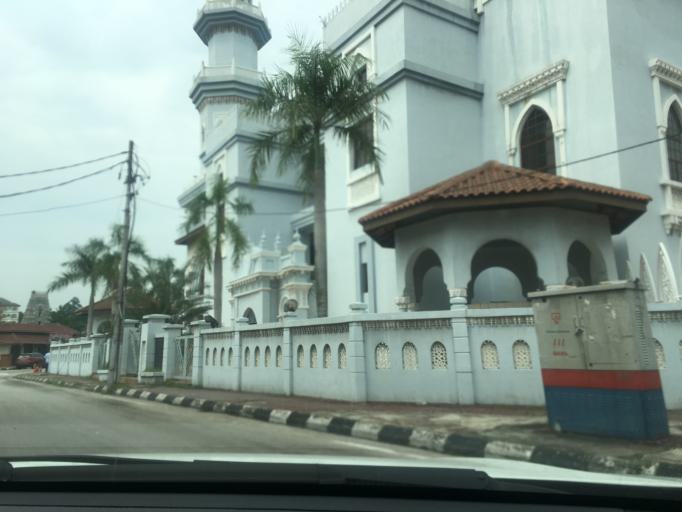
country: MY
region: Selangor
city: Klang
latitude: 3.0416
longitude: 101.4473
